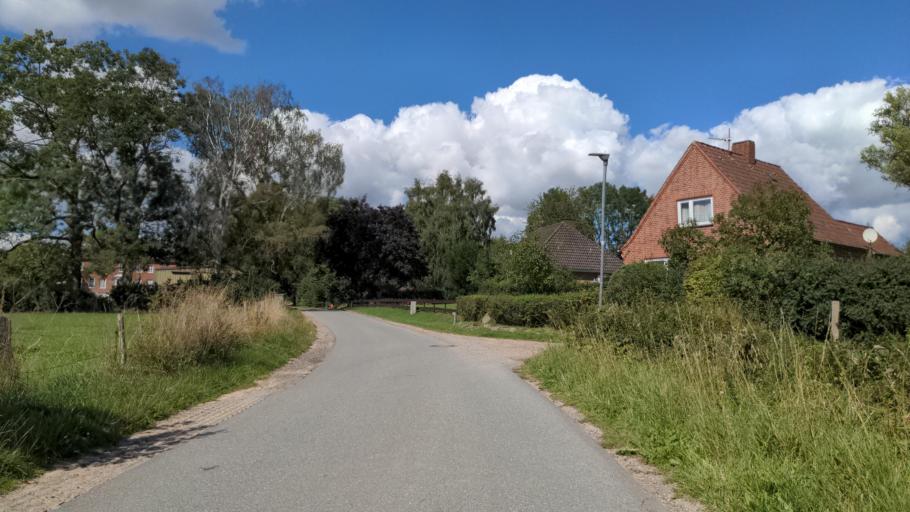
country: DE
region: Schleswig-Holstein
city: Beschendorf
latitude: 54.1770
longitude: 10.8438
